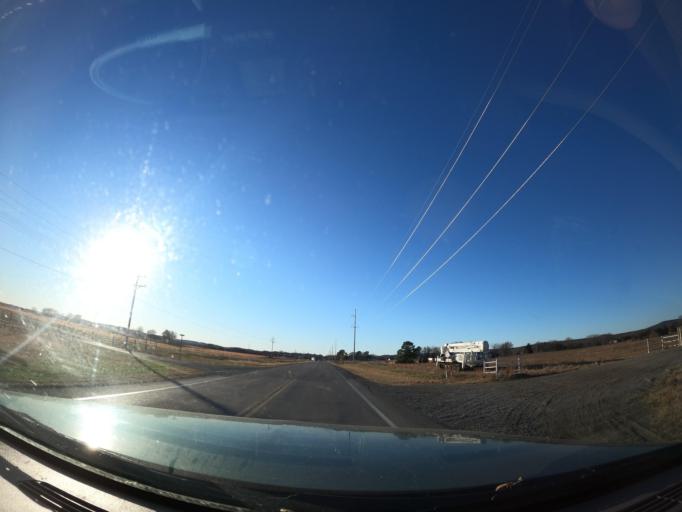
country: US
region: Oklahoma
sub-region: Latimer County
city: Wilburton
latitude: 34.9129
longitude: -95.4136
